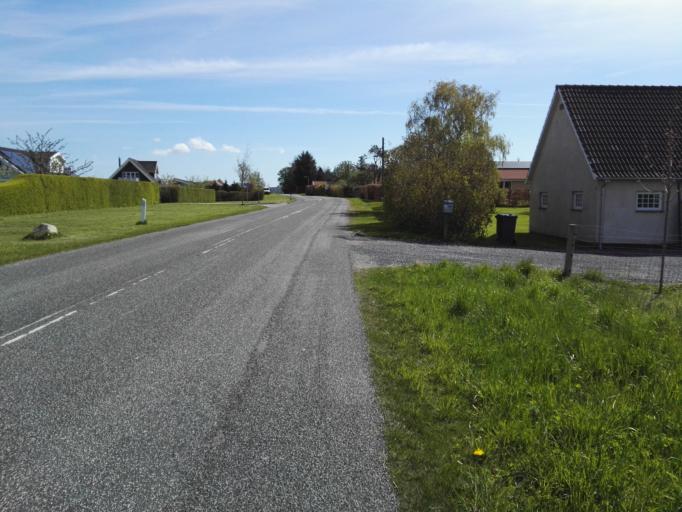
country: DK
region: Capital Region
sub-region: Halsnaes Kommune
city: Frederiksvaerk
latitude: 55.9691
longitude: 11.9825
